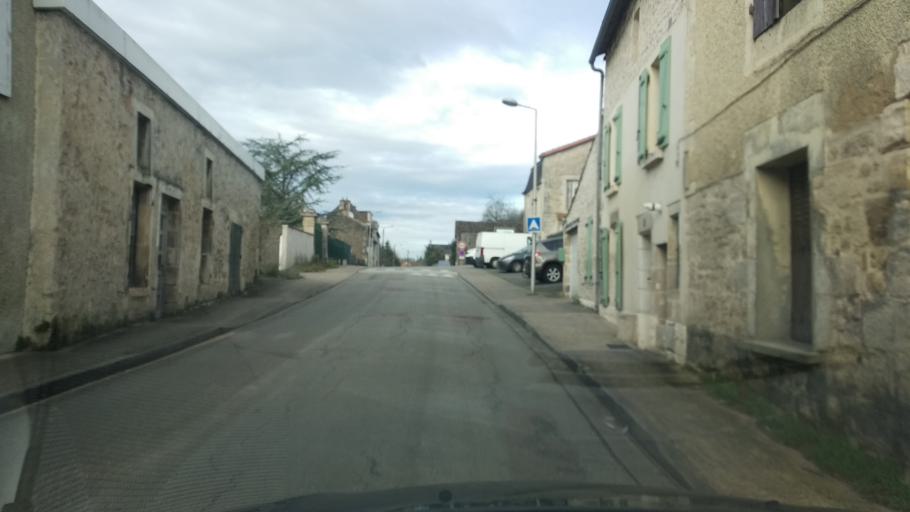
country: FR
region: Poitou-Charentes
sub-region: Departement de la Vienne
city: Poitiers
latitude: 46.6112
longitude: 0.3557
